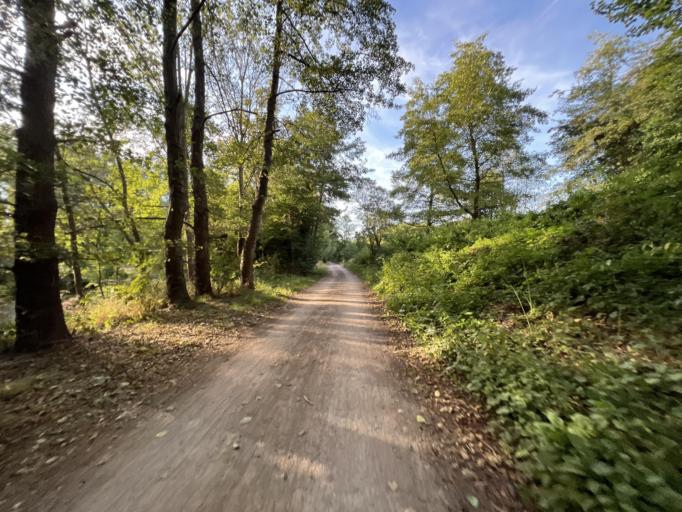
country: DE
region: North Rhine-Westphalia
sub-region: Regierungsbezirk Koln
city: Dueren
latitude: 50.8076
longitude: 6.4635
